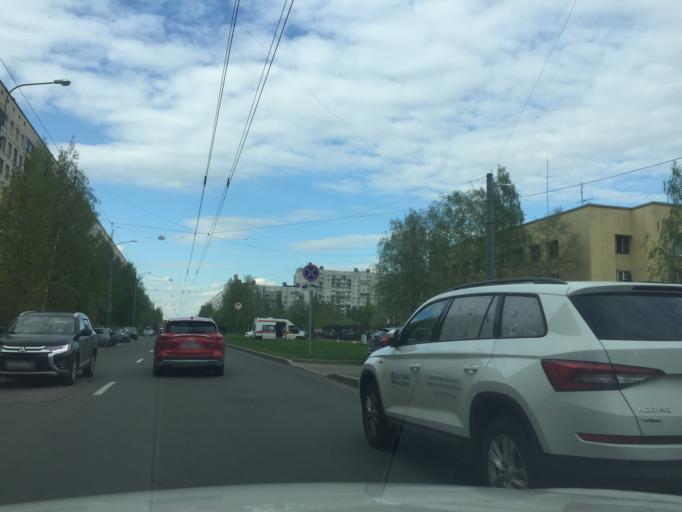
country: RU
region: Leningrad
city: Parnas
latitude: 60.0527
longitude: 30.3430
